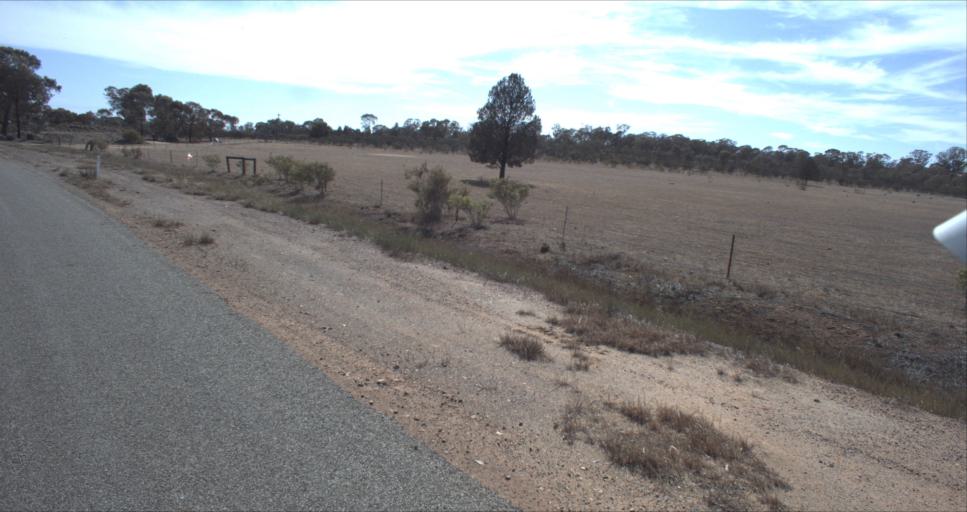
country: AU
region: New South Wales
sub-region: Leeton
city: Leeton
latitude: -34.5823
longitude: 146.4768
